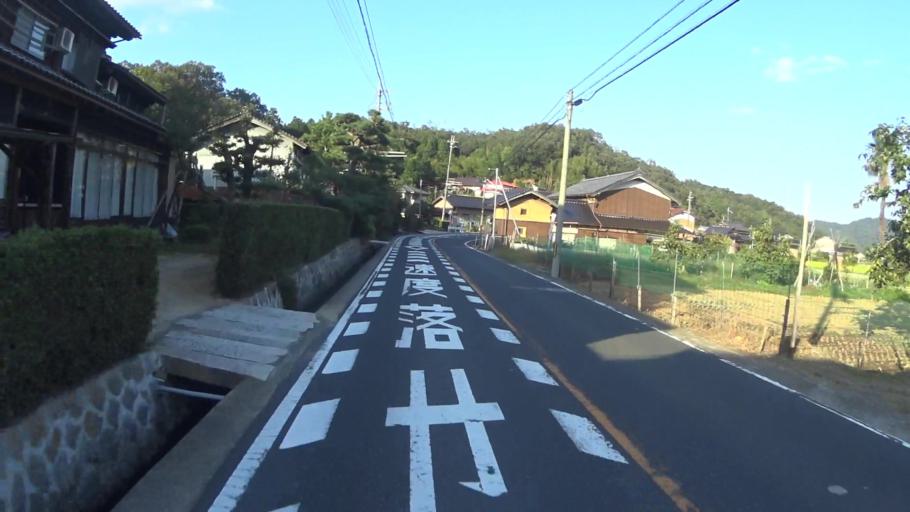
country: JP
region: Kyoto
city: Miyazu
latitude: 35.5792
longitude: 135.0214
